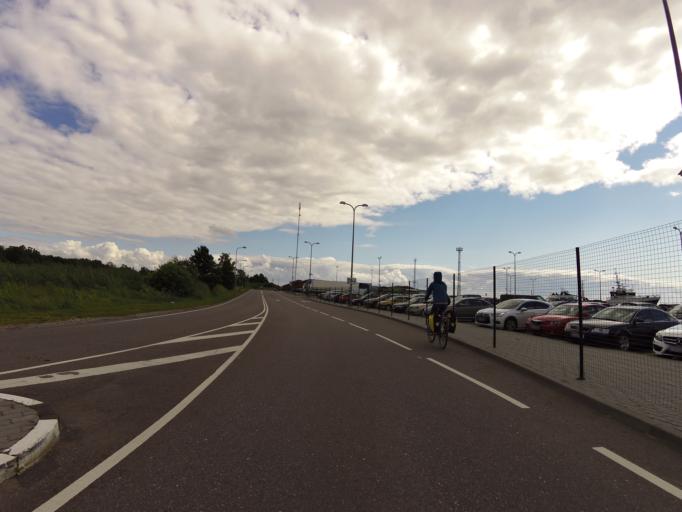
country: EE
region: Laeaene
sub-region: Haapsalu linn
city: Haapsalu
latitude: 58.9063
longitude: 23.4259
